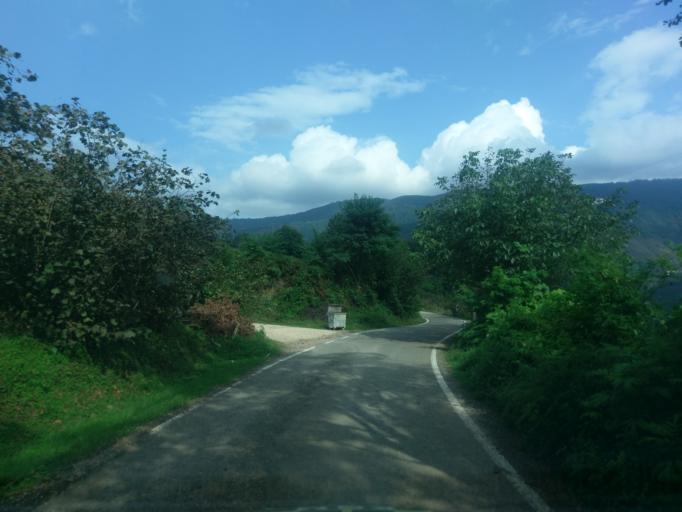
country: TR
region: Ordu
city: Camas
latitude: 40.9273
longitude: 37.6159
